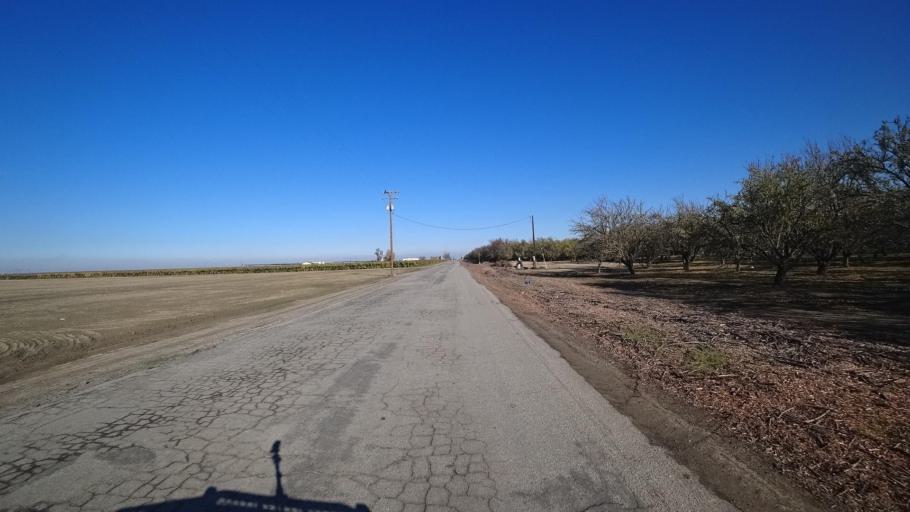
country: US
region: California
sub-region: Kern County
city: McFarland
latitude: 35.6842
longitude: -119.2675
